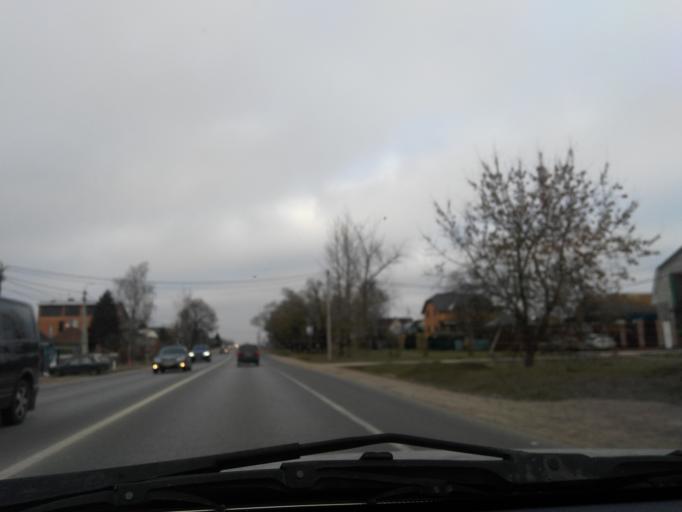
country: RU
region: Moskovskaya
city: Troitsk
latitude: 55.3245
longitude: 37.1622
